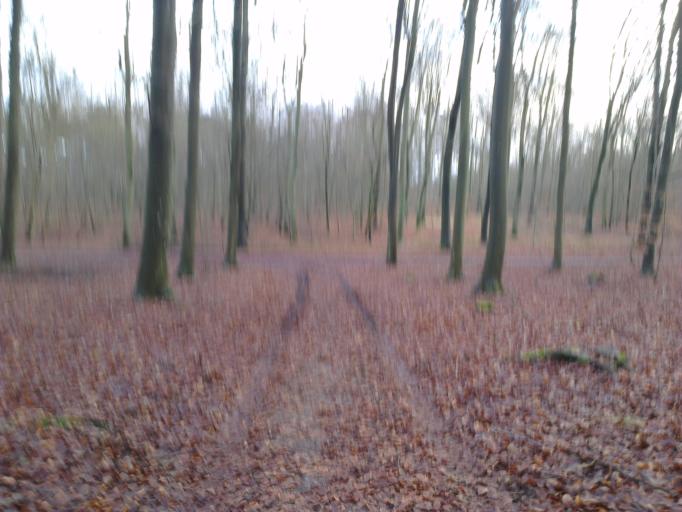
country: DK
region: Capital Region
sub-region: Frederikssund Kommune
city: Frederikssund
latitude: 55.8454
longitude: 12.0218
